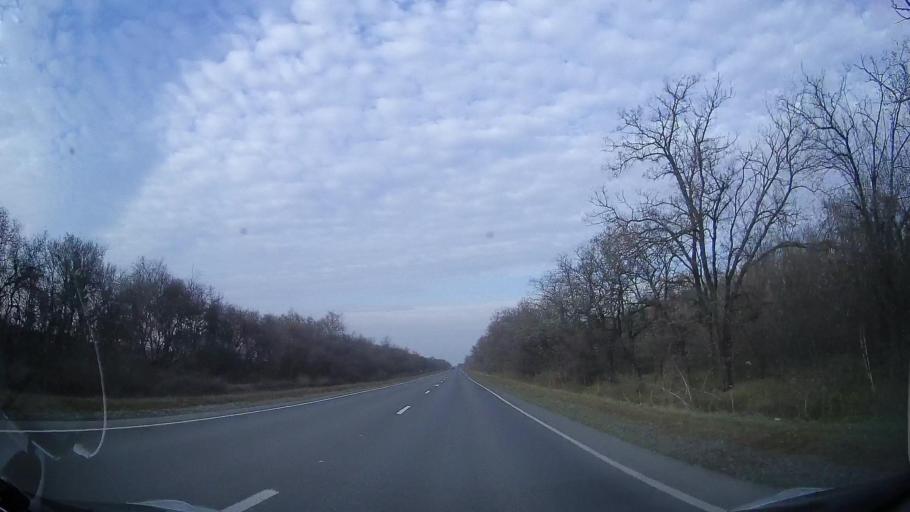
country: RU
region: Rostov
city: Bagayevskaya
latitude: 47.1272
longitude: 40.2767
